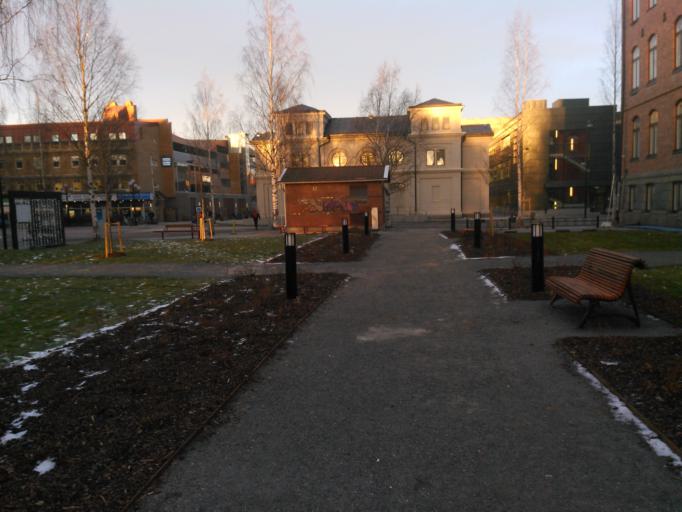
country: SE
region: Vaesterbotten
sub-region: Umea Kommun
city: Umea
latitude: 63.8254
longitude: 20.2687
